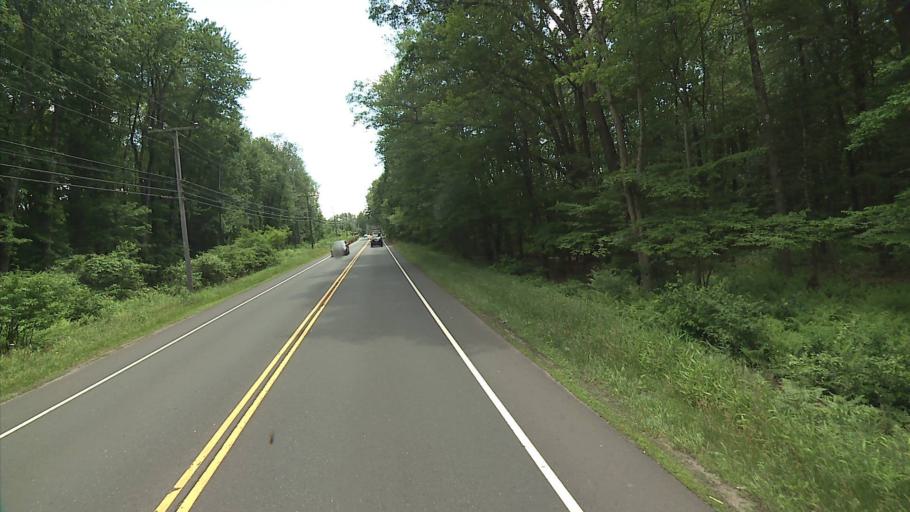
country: US
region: Connecticut
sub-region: Litchfield County
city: Oakville
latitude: 41.5586
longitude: -73.0935
